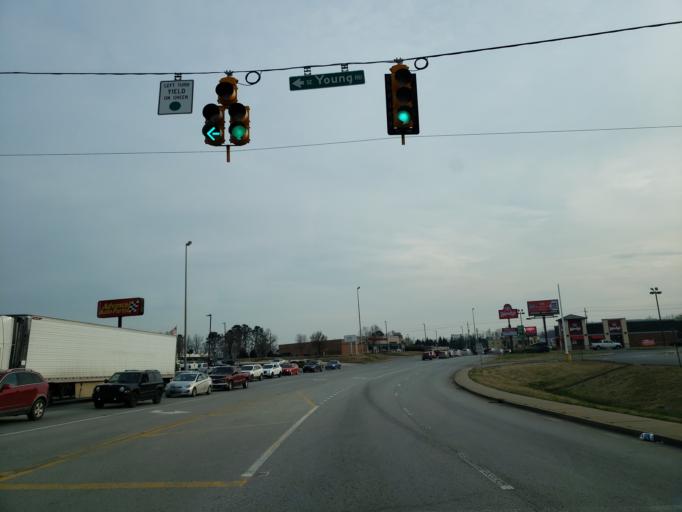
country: US
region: Tennessee
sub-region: Bradley County
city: South Cleveland
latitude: 35.1300
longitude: -84.8651
